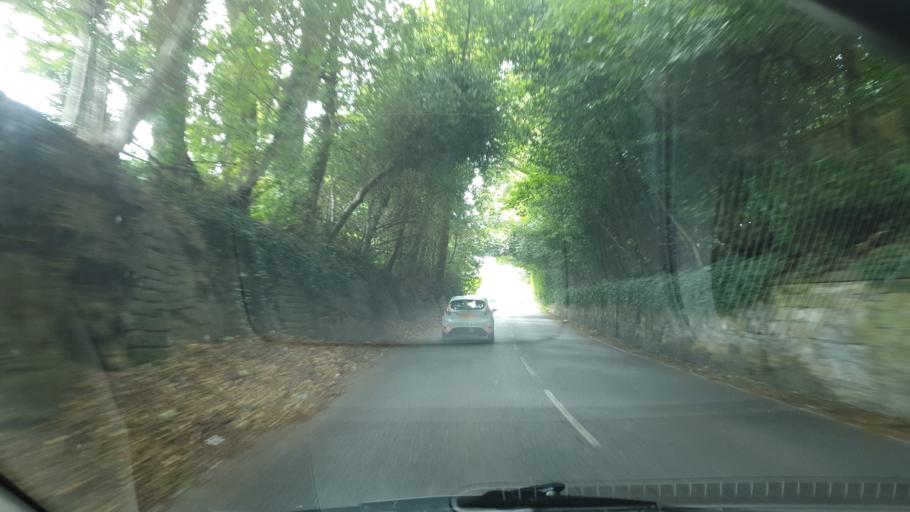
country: GB
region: England
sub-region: West Sussex
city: East Grinstead
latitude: 51.1282
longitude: -0.0037
